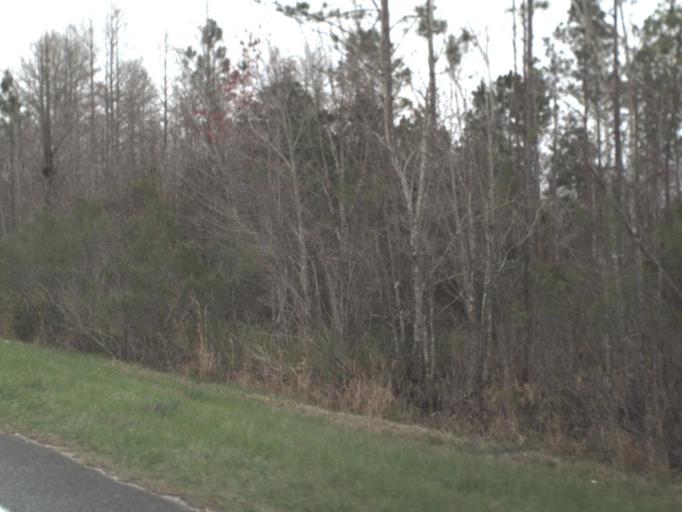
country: US
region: Florida
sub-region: Leon County
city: Woodville
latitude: 30.1941
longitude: -84.1291
